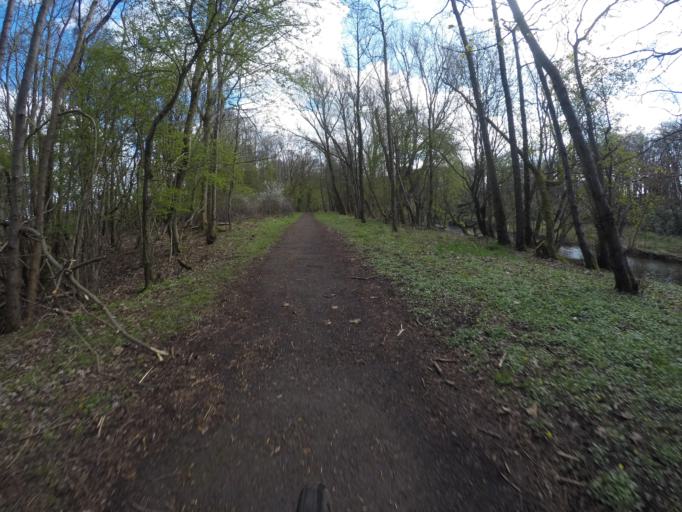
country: GB
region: Scotland
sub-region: North Ayrshire
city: Dreghorn
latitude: 55.5978
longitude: -4.6299
